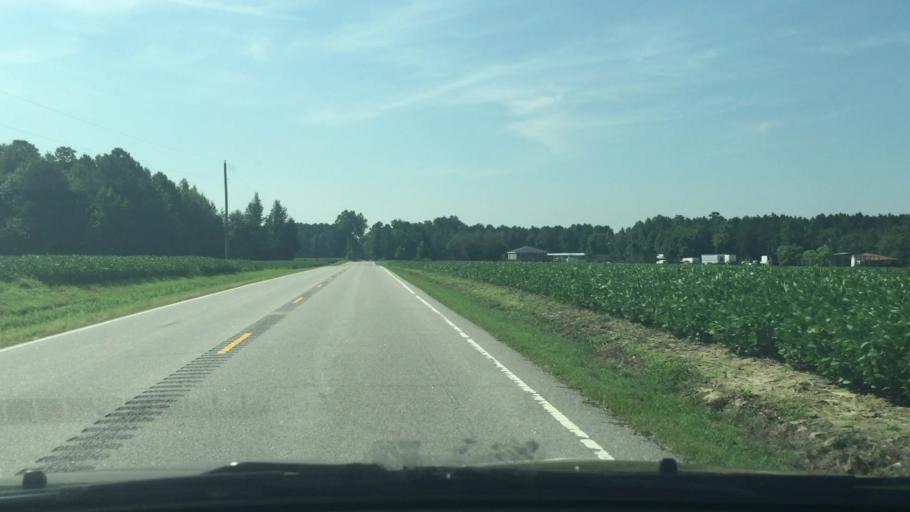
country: US
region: Virginia
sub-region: Southampton County
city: Courtland
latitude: 36.8291
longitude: -77.1270
